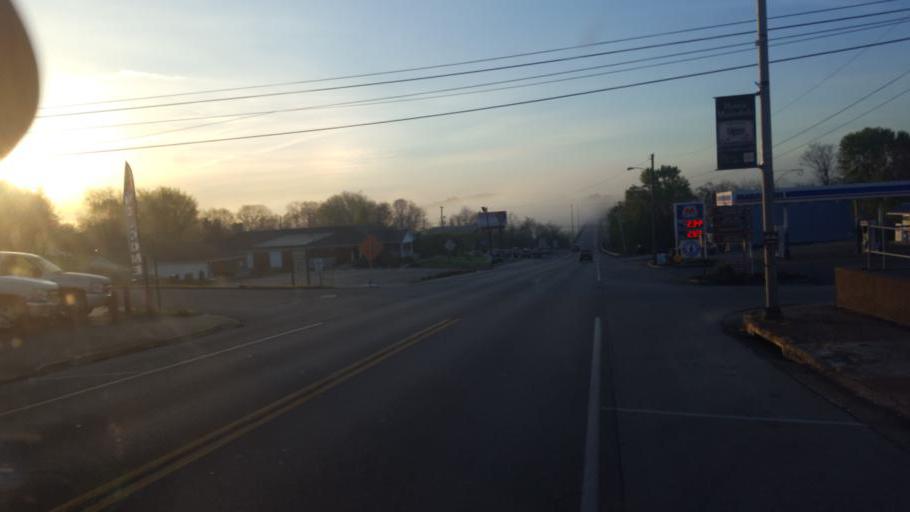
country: US
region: Kentucky
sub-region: Hart County
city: Munfordville
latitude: 37.2708
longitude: -85.8891
